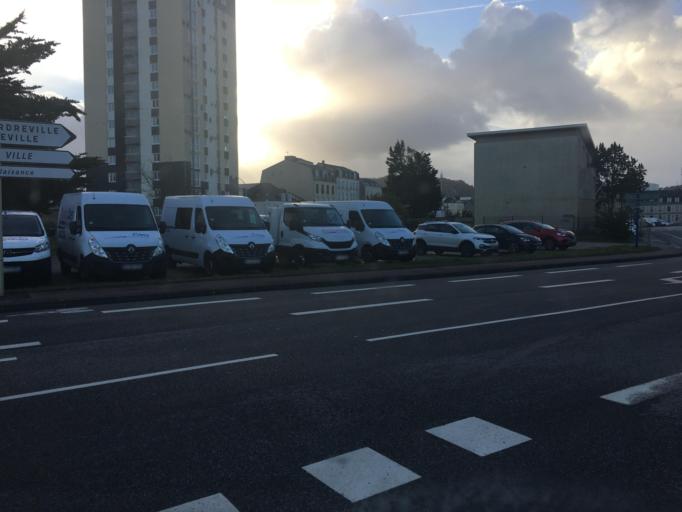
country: FR
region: Lower Normandy
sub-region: Departement de la Manche
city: Cherbourg-Octeville
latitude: 49.6419
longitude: -1.6178
